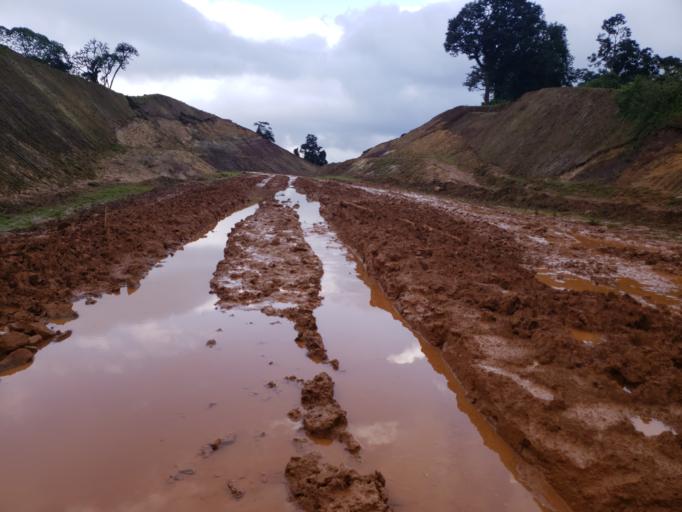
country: ET
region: Oromiya
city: Dodola
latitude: 6.6681
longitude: 39.3662
